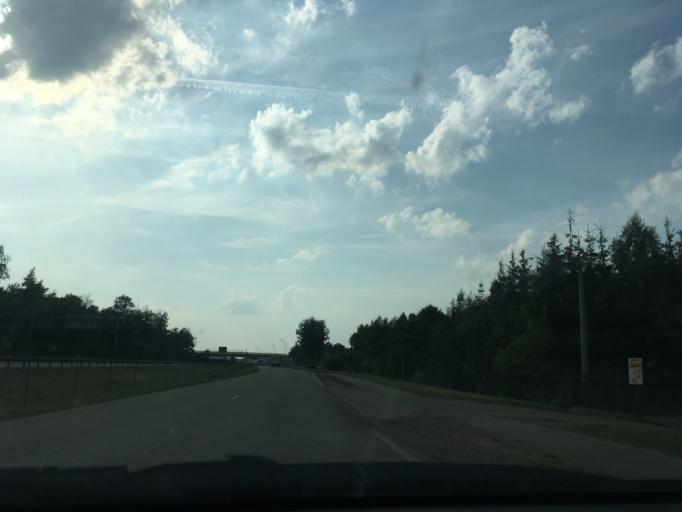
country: PL
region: Podlasie
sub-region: Powiat bialostocki
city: Choroszcz
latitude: 53.1564
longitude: 23.0166
